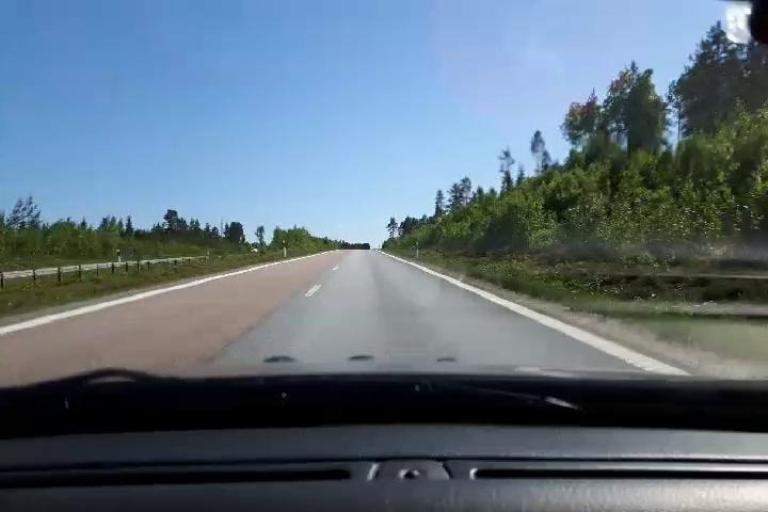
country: SE
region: Gaevleborg
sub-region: Soderhamns Kommun
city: Soderhamn
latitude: 61.3952
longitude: 16.9919
